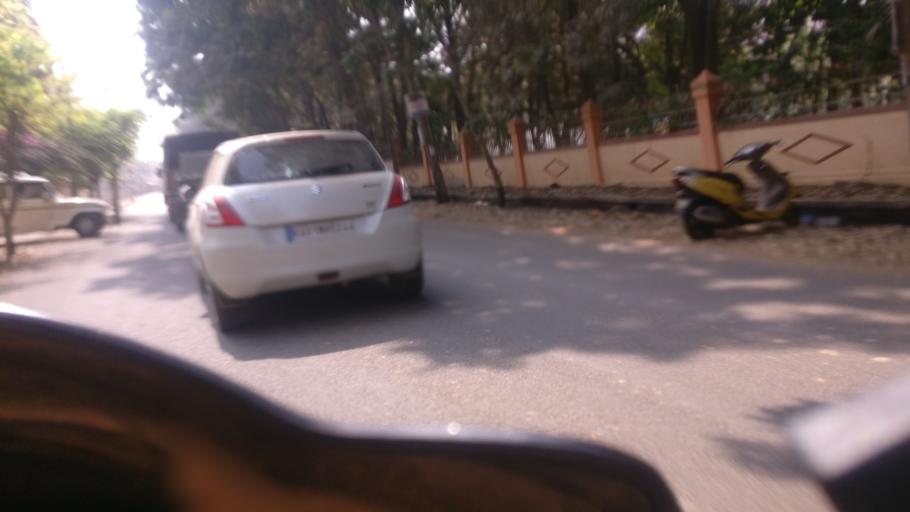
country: IN
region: Karnataka
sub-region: Bangalore Urban
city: Bangalore
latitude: 12.8953
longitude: 77.6758
